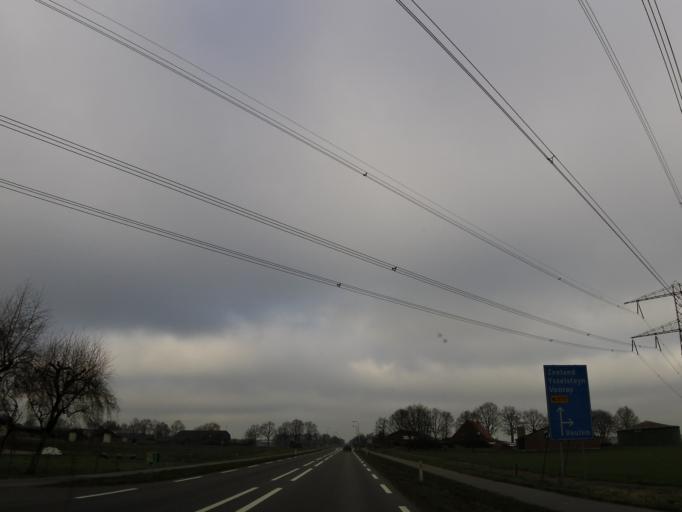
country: NL
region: Limburg
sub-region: Gemeente Venray
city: Venray
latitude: 51.4711
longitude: 5.9310
